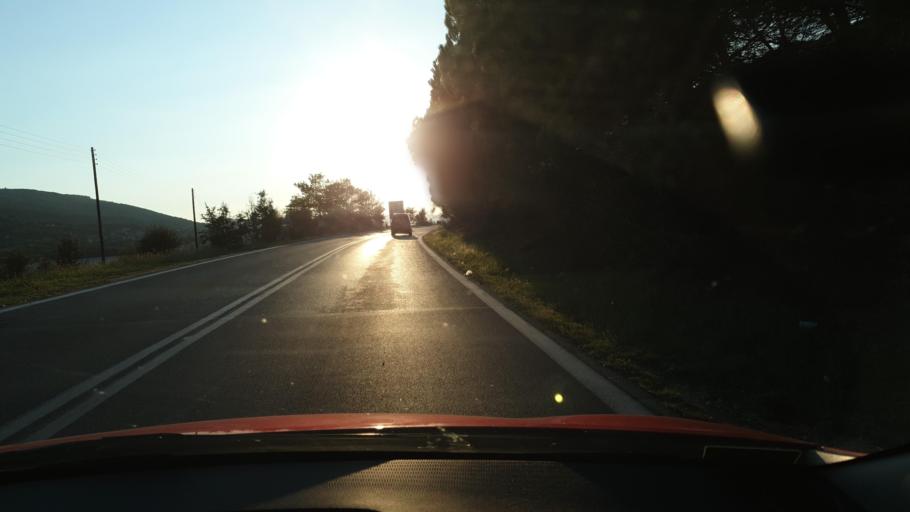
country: GR
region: Central Macedonia
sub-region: Nomos Thessalonikis
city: Nea Apollonia
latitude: 40.5051
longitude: 23.4722
